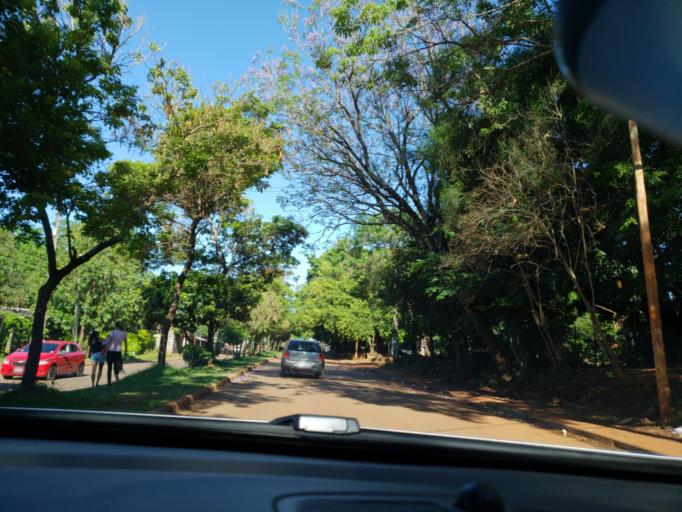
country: AR
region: Misiones
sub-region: Departamento de Capital
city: Posadas
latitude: -27.3840
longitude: -55.9337
